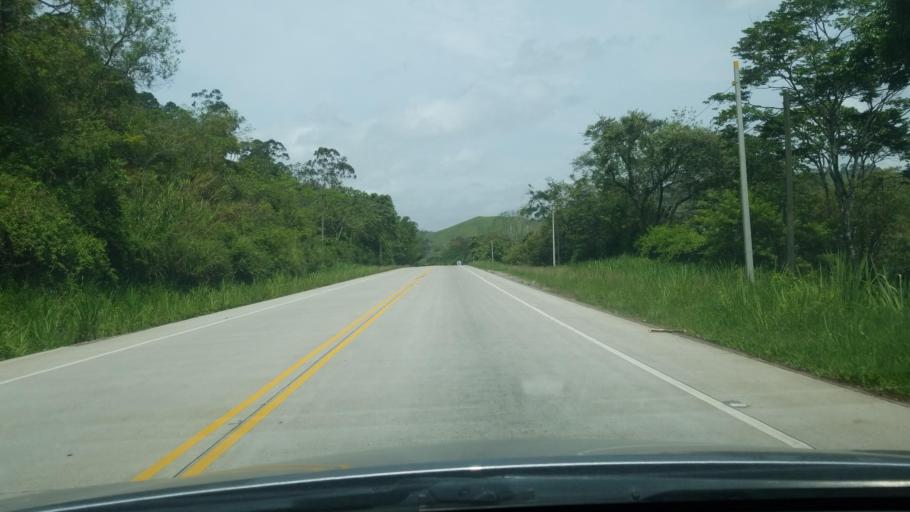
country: HN
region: Copan
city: Agua Caliente
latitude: 14.8598
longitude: -88.7935
